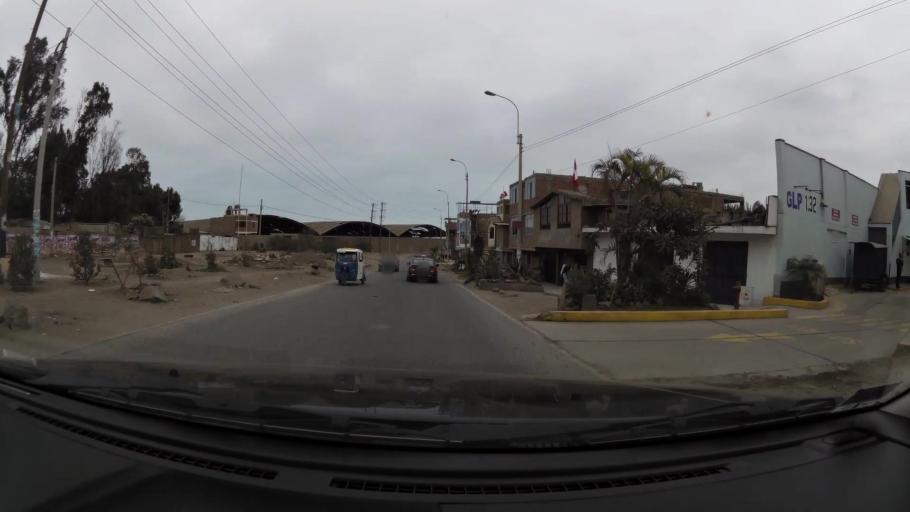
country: PE
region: Lima
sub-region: Lima
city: Surco
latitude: -12.1984
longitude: -76.9584
